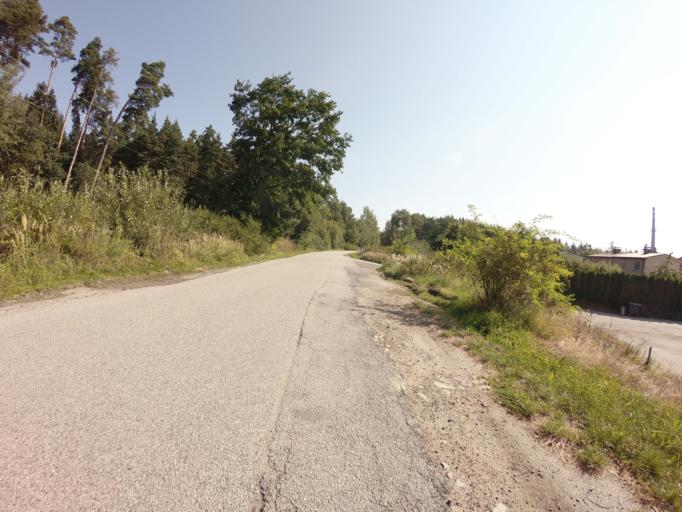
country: CZ
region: Jihocesky
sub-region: Okres Cesky Krumlov
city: Cesky Krumlov
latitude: 48.8367
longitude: 14.3300
